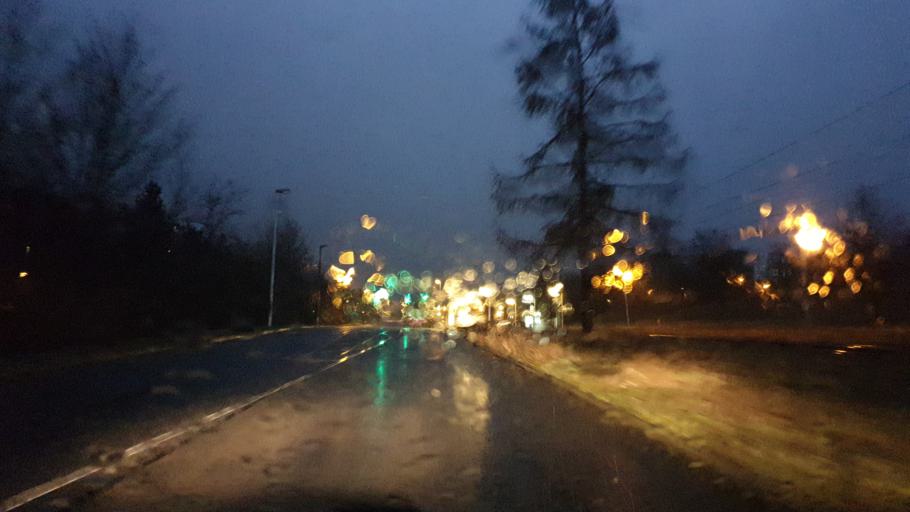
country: DE
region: Thuringia
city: Gera
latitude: 50.9031
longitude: 12.0907
